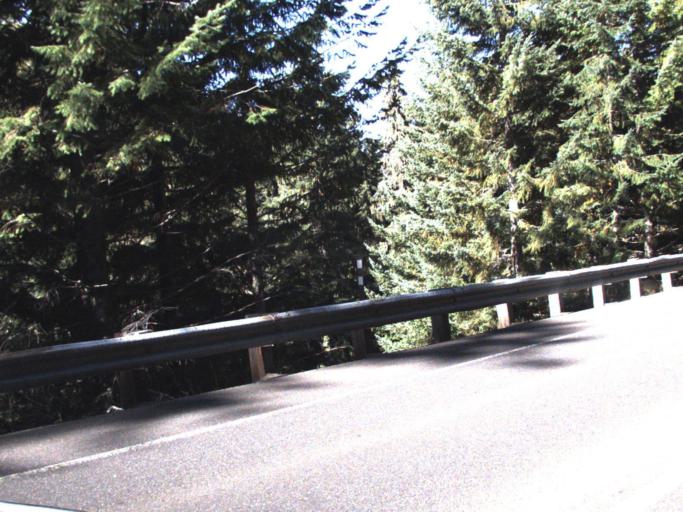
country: US
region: Washington
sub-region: Yakima County
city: Tieton
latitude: 46.6582
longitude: -121.4758
